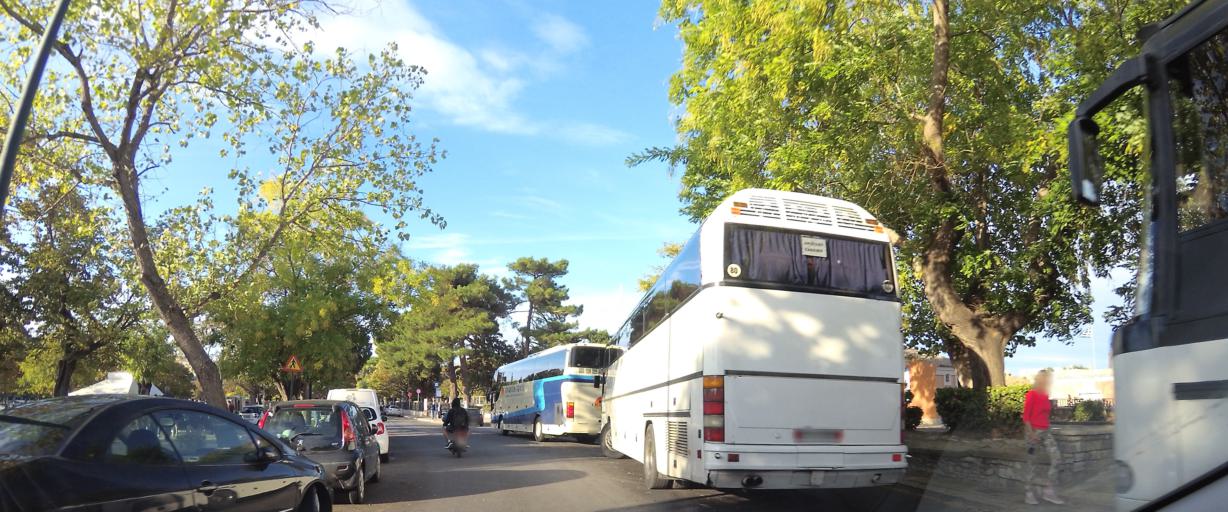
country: GR
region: Ionian Islands
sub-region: Nomos Kerkyras
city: Kerkyra
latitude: 39.6232
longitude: 19.9255
